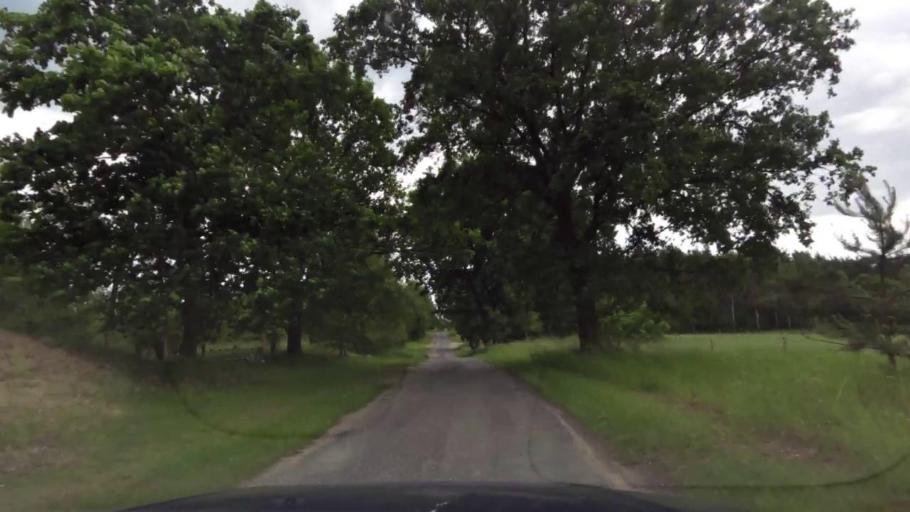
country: PL
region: West Pomeranian Voivodeship
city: Trzcinsko Zdroj
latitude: 52.8759
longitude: 14.5839
